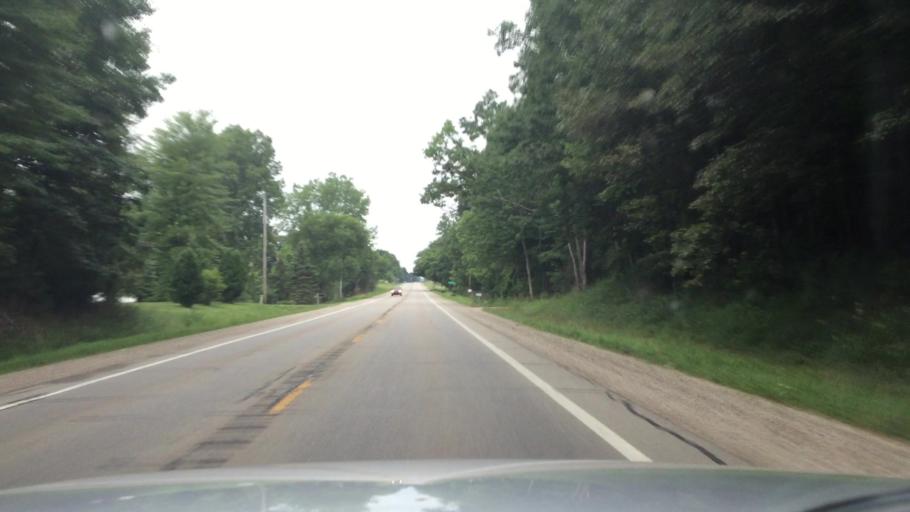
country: US
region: Michigan
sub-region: Montcalm County
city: Greenville
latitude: 43.1706
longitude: -85.1379
